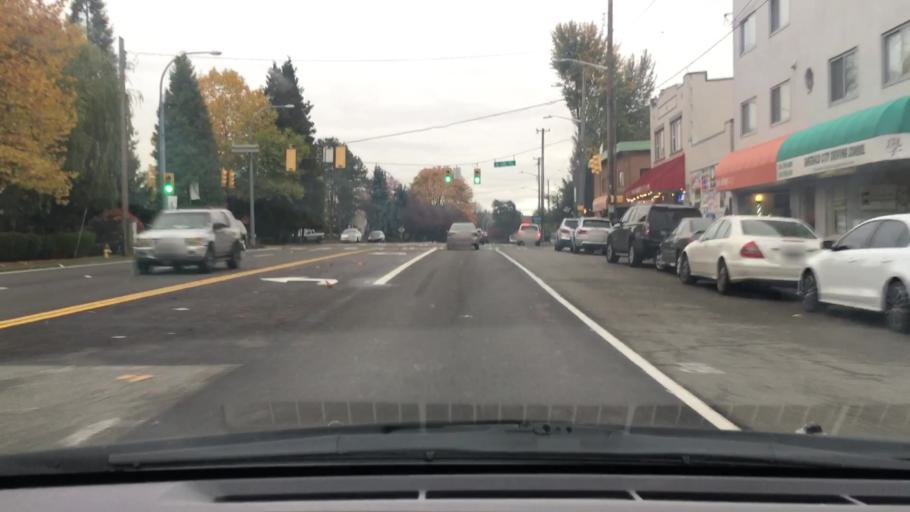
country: US
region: Washington
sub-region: King County
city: Renton
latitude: 47.5001
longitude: -122.2212
